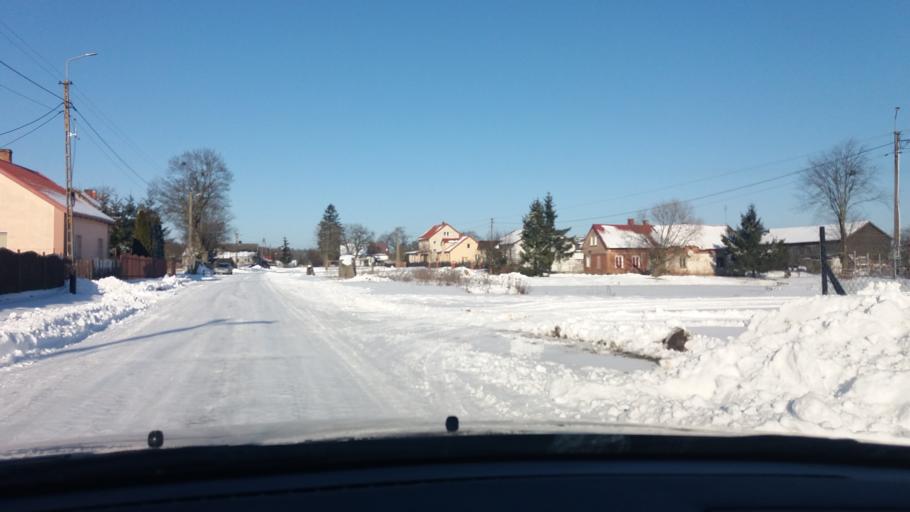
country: PL
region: Warmian-Masurian Voivodeship
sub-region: Powiat nidzicki
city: Nidzica
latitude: 53.3778
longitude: 20.6082
